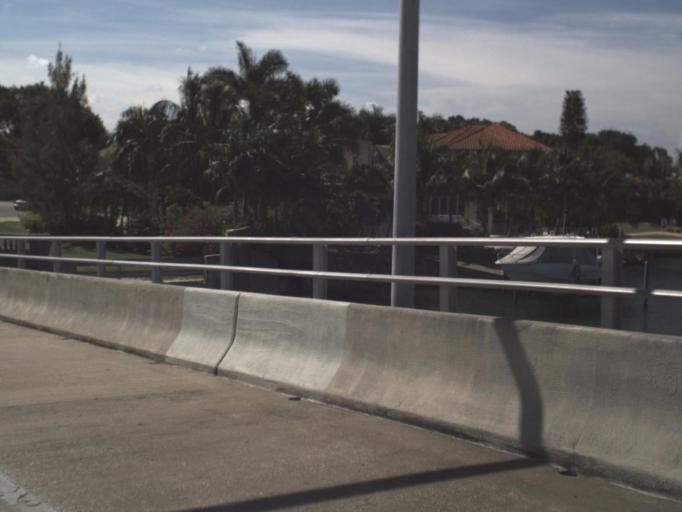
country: US
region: Florida
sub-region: Sarasota County
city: Siesta Key
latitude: 27.3326
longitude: -82.5814
